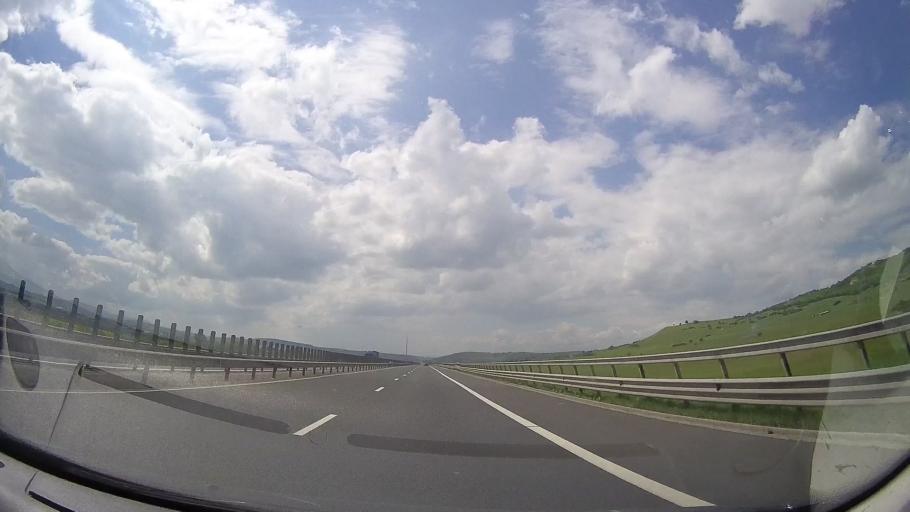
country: RO
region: Sibiu
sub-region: Oras Miercurea Sibiului
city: Miercurea Sibiului
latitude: 45.8937
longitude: 23.8195
